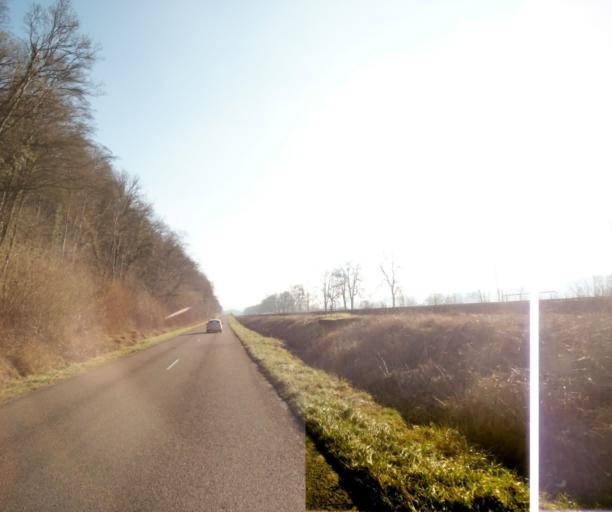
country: FR
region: Champagne-Ardenne
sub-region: Departement de la Haute-Marne
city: Chevillon
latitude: 48.5122
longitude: 5.1206
